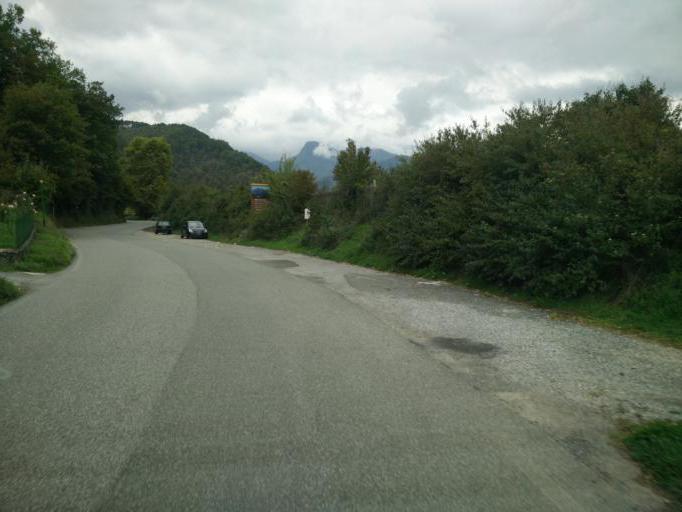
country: IT
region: Tuscany
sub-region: Provincia di Massa-Carrara
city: Fivizzano
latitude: 44.1973
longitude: 10.1066
